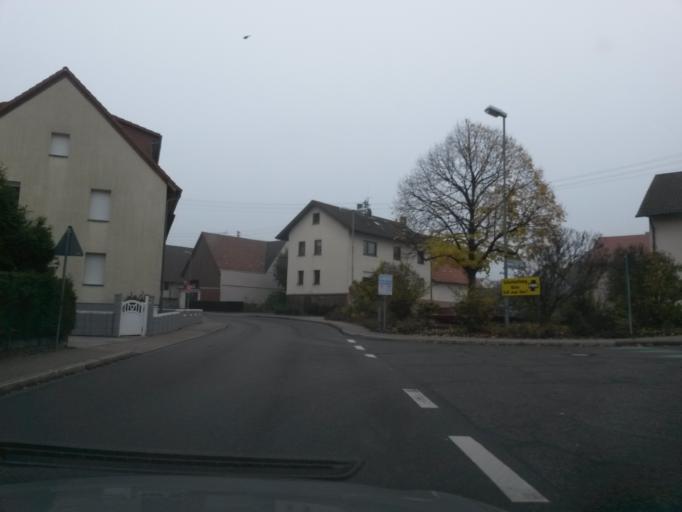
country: DE
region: Baden-Wuerttemberg
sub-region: Karlsruhe Region
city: Ettlingen
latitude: 48.8969
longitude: 8.4684
